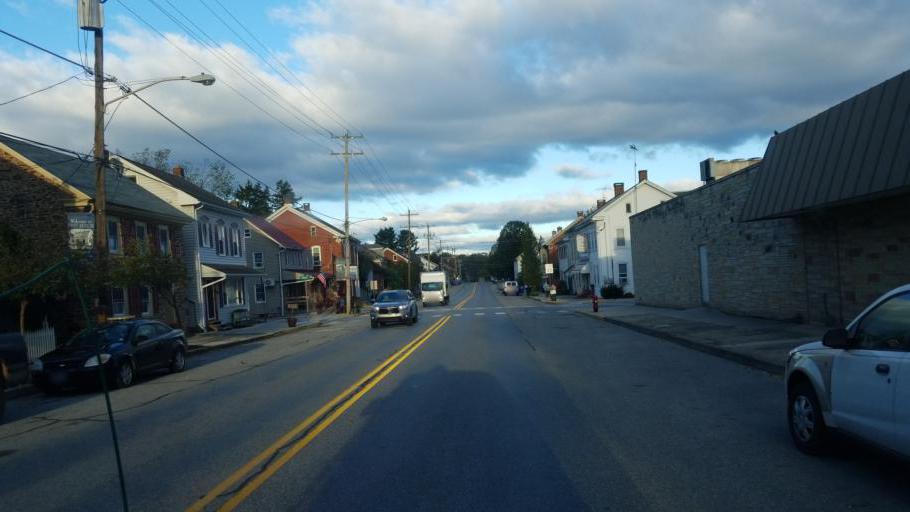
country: US
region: Pennsylvania
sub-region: Adams County
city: East Berlin
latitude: 39.9397
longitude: -76.9845
